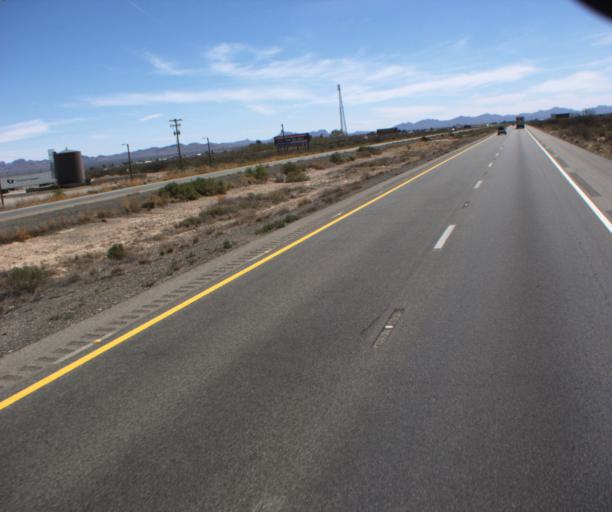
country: US
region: New Mexico
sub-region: Hidalgo County
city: Lordsburg
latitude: 32.2693
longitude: -109.2446
